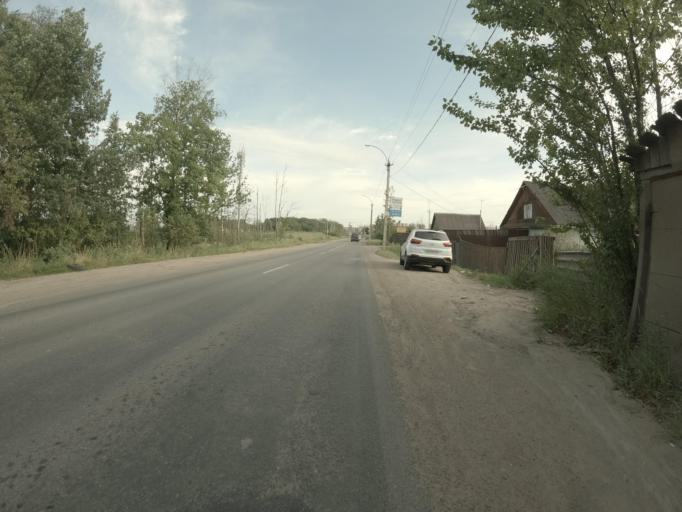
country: RU
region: St.-Petersburg
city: Krasnogvargeisky
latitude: 59.9336
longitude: 30.5204
